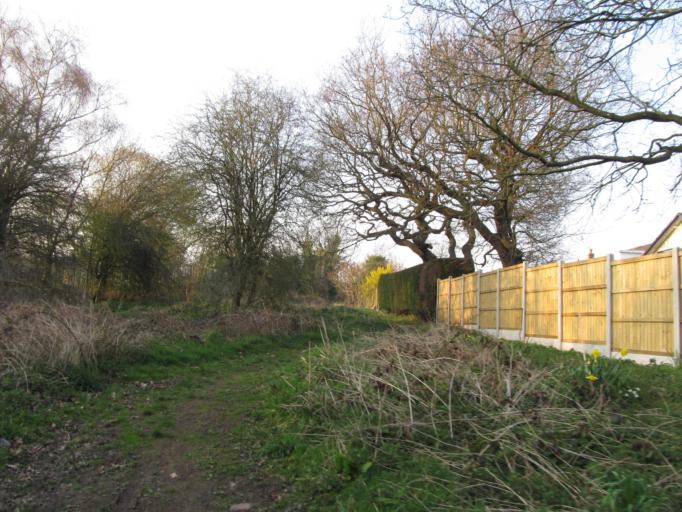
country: GB
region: Wales
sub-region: County of Flintshire
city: Buckley
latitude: 53.2002
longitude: -3.0900
